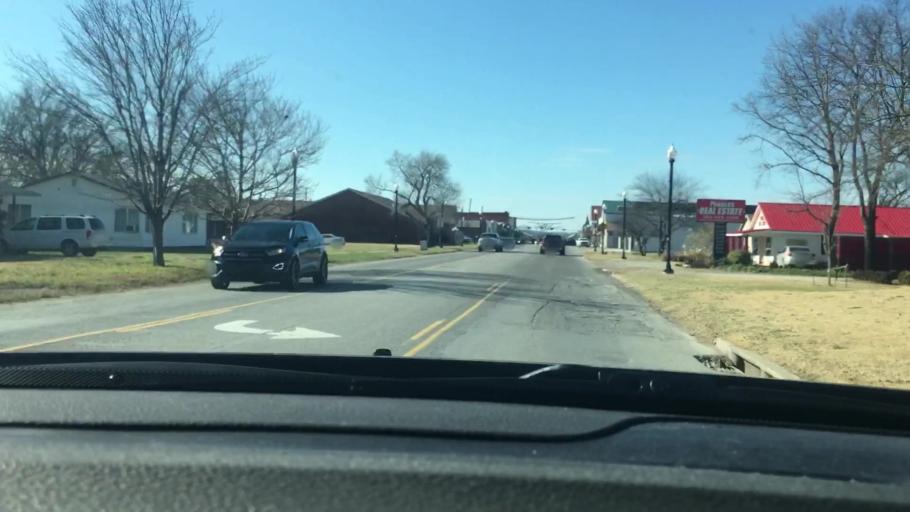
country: US
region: Oklahoma
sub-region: Murray County
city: Davis
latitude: 34.5057
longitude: -97.1162
